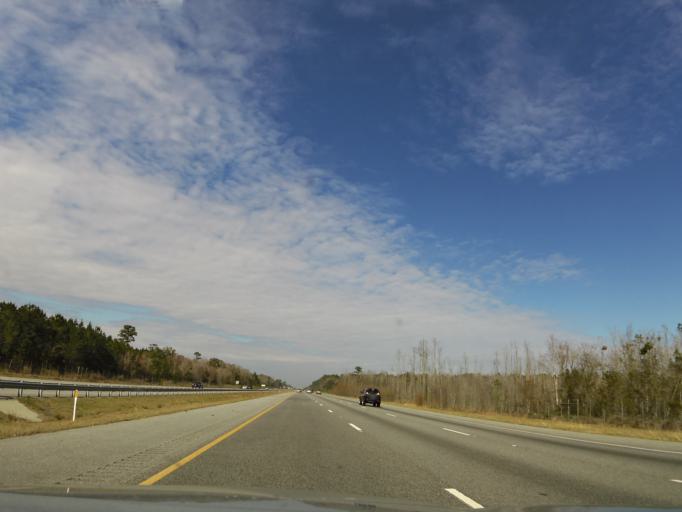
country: US
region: Georgia
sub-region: McIntosh County
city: Darien
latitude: 31.4954
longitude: -81.4466
